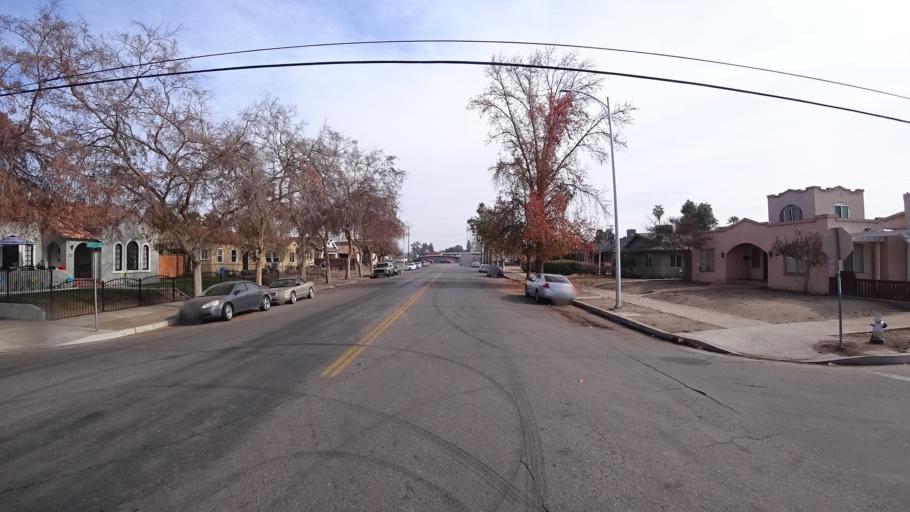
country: US
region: California
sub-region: Kern County
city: Bakersfield
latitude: 35.3743
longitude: -119.0048
